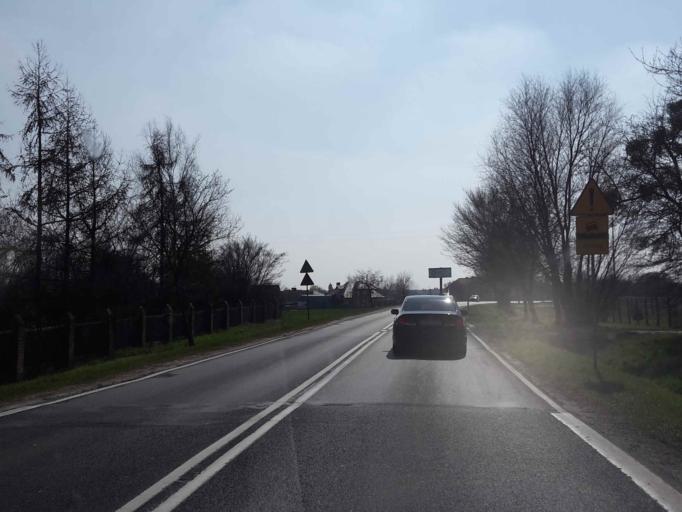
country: PL
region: Kujawsko-Pomorskie
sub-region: Powiat golubsko-dobrzynski
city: Kowalewo Pomorskie
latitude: 53.1190
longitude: 18.8319
